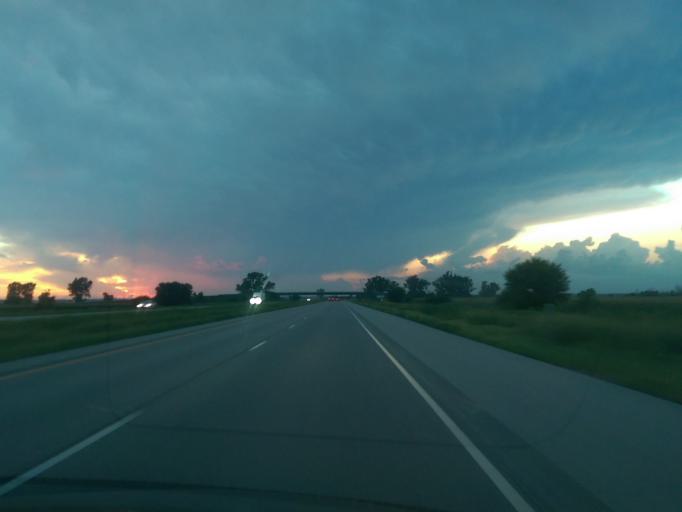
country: US
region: Nebraska
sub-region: Otoe County
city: Nebraska City
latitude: 40.7200
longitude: -95.8076
